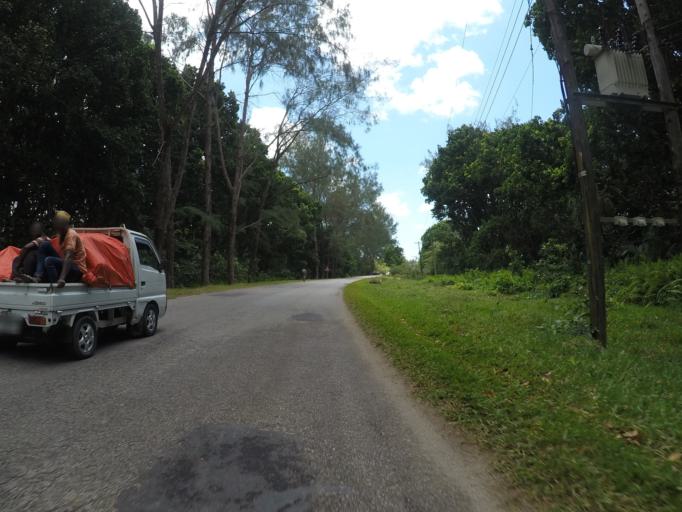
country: TZ
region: Zanzibar Central/South
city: Mahonda
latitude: -6.2774
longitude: 39.4153
